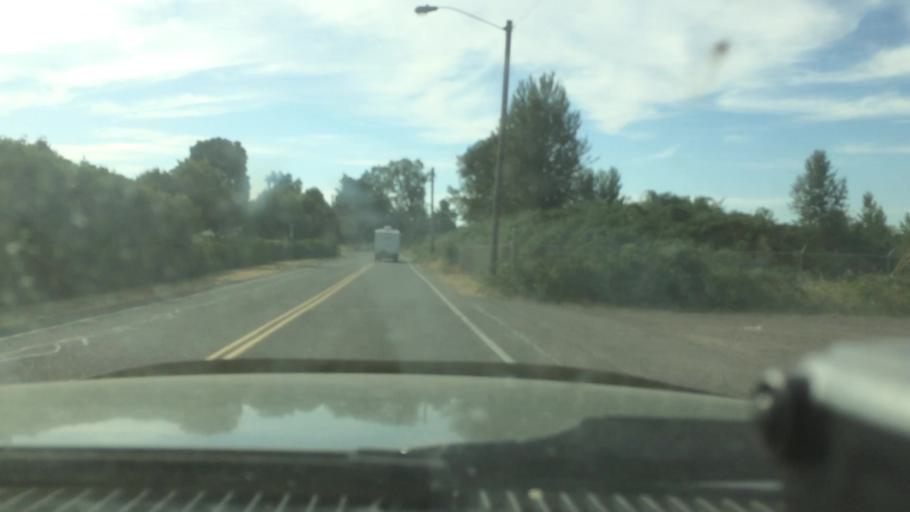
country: US
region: Oregon
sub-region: Lane County
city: Eugene
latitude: 44.1024
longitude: -123.1155
